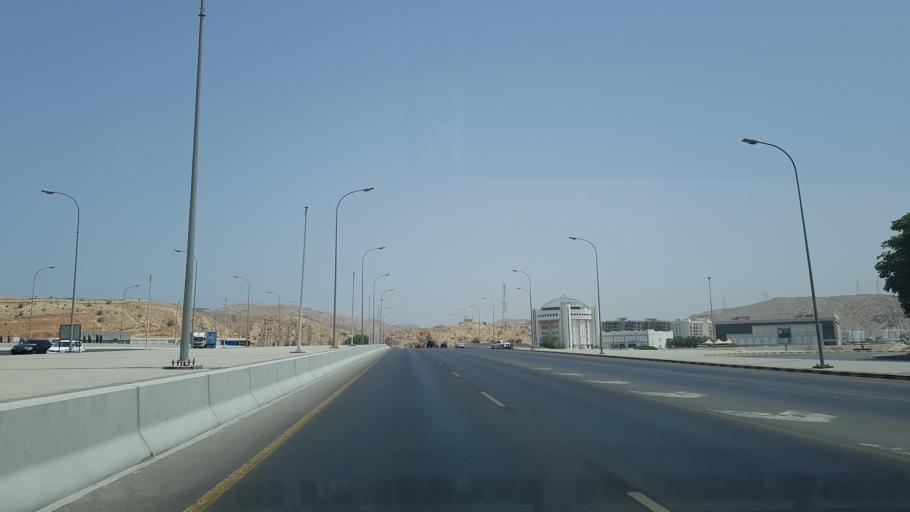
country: OM
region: Muhafazat Masqat
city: Muscat
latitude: 23.6101
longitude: 58.4961
